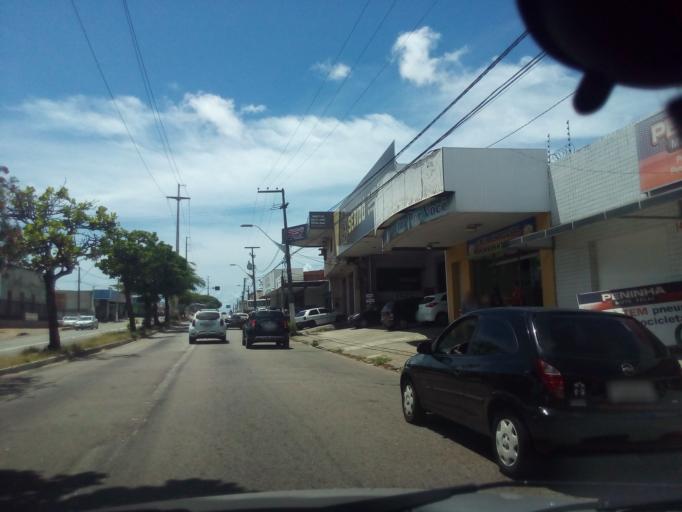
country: BR
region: Rio Grande do Norte
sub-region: Natal
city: Natal
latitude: -5.8051
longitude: -35.2261
